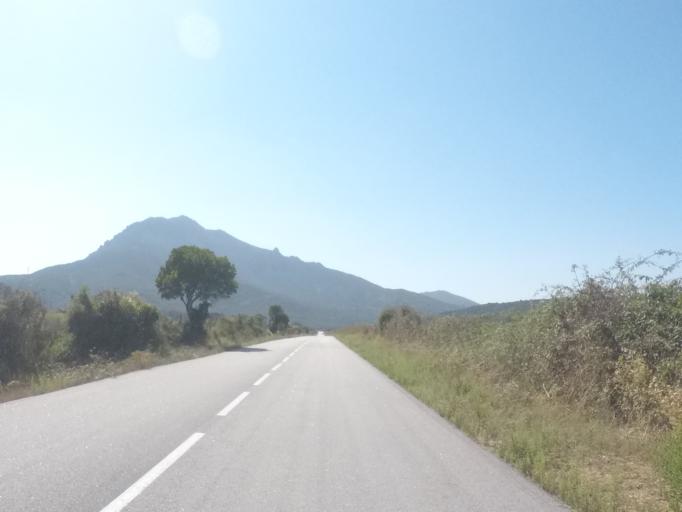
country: FR
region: Corsica
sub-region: Departement de la Haute-Corse
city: Calvi
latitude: 42.4175
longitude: 8.7112
